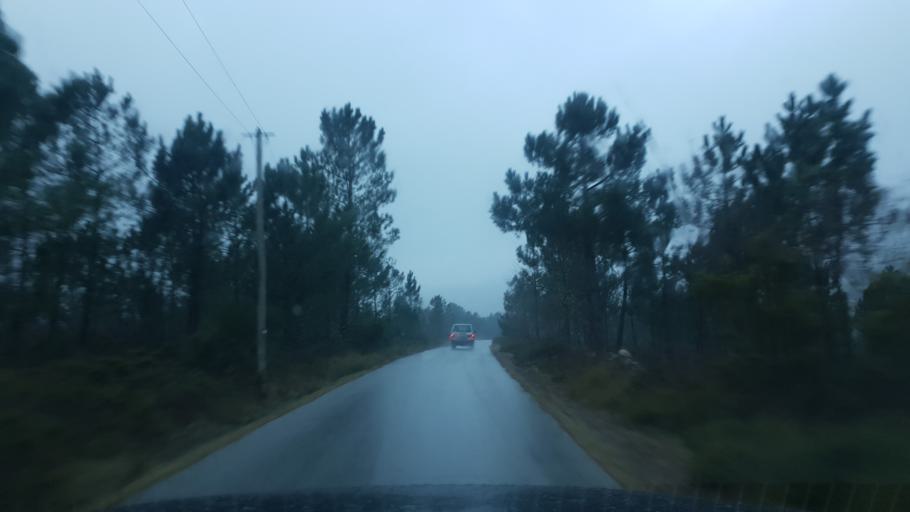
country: PT
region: Viseu
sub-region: Oliveira de Frades
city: Oliveira de Frades
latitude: 40.8273
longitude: -8.1419
